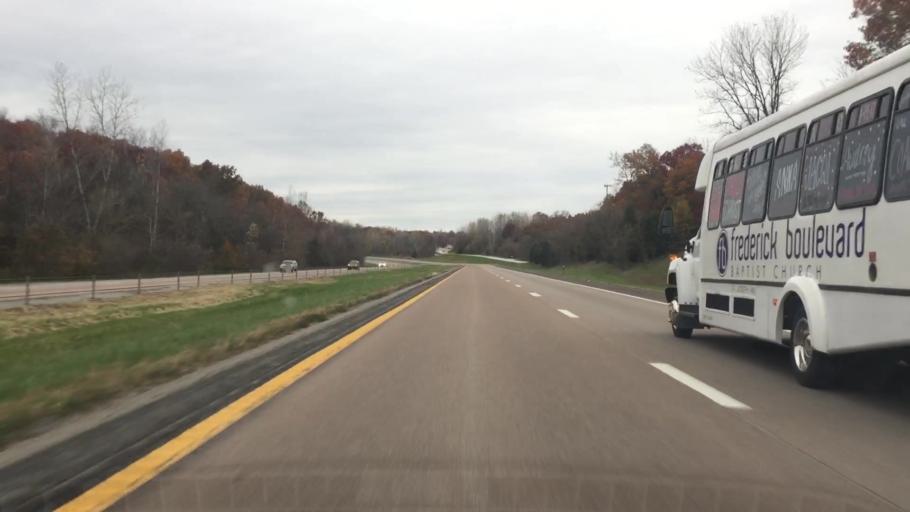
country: US
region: Missouri
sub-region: Cole County
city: Jefferson City
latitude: 38.6644
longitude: -92.2265
